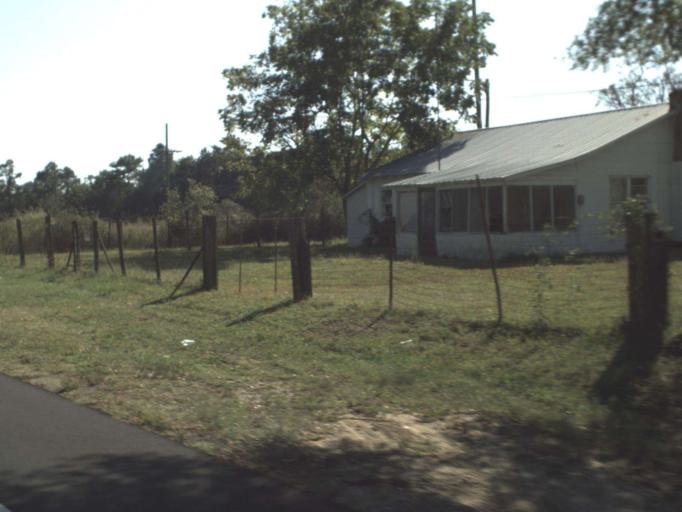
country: US
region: Florida
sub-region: Walton County
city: DeFuniak Springs
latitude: 30.7501
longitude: -86.1483
